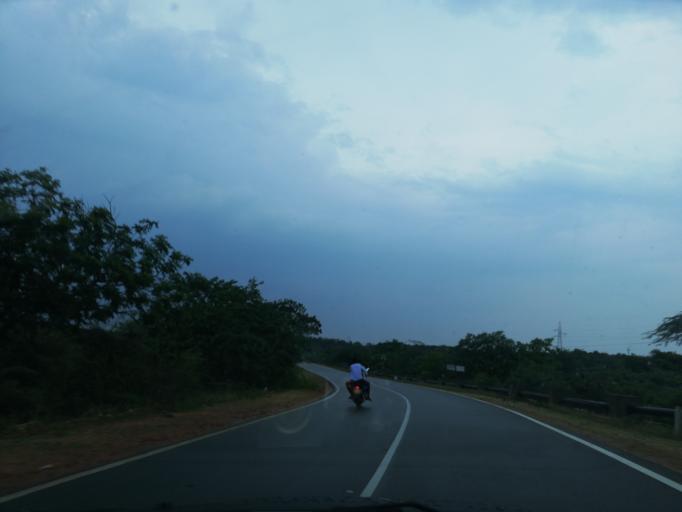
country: IN
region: Andhra Pradesh
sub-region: Guntur
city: Macherla
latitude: 16.6569
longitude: 79.2851
